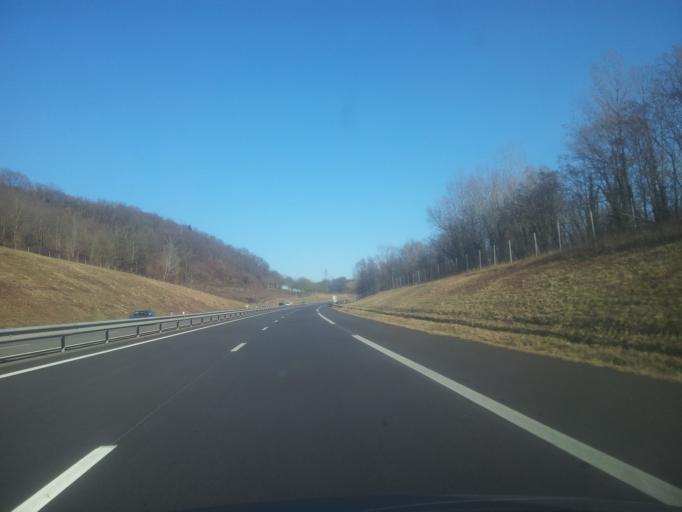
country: FR
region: Rhone-Alpes
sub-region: Departement de l'Isere
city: Saint-Hilaire-du-Rosier
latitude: 45.0957
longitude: 5.2246
